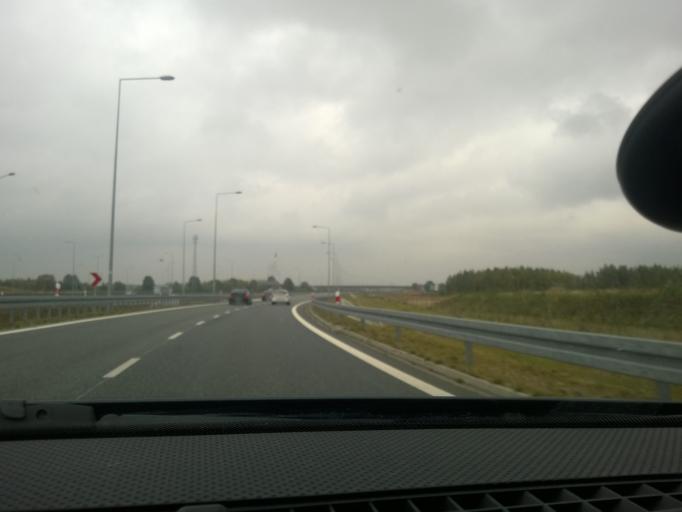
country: PL
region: Lodz Voivodeship
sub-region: Powiat zgierski
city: Strykow
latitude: 51.8913
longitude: 19.6414
